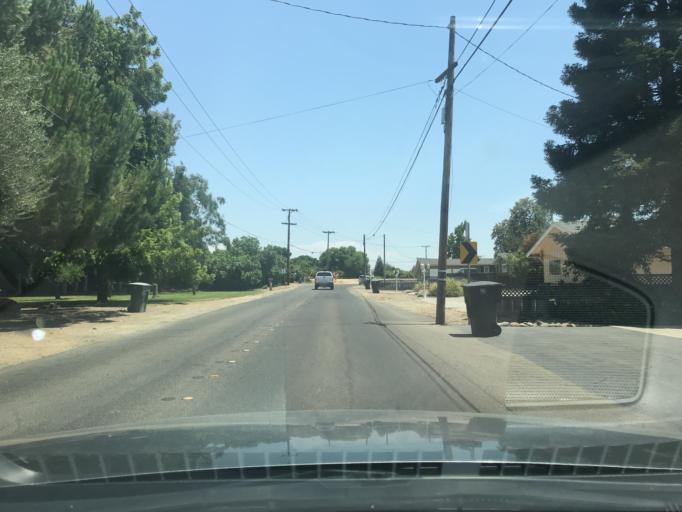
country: US
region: California
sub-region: Merced County
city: Atwater
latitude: 37.3641
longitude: -120.6005
